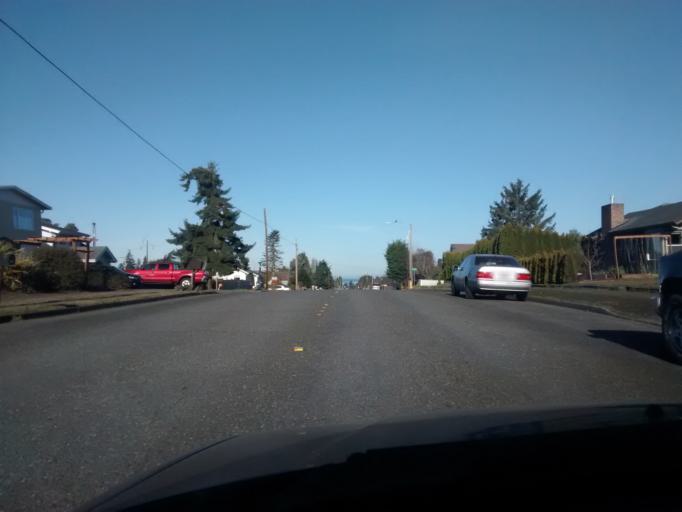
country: US
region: Washington
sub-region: Clallam County
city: Port Angeles
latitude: 48.1241
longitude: -123.4576
